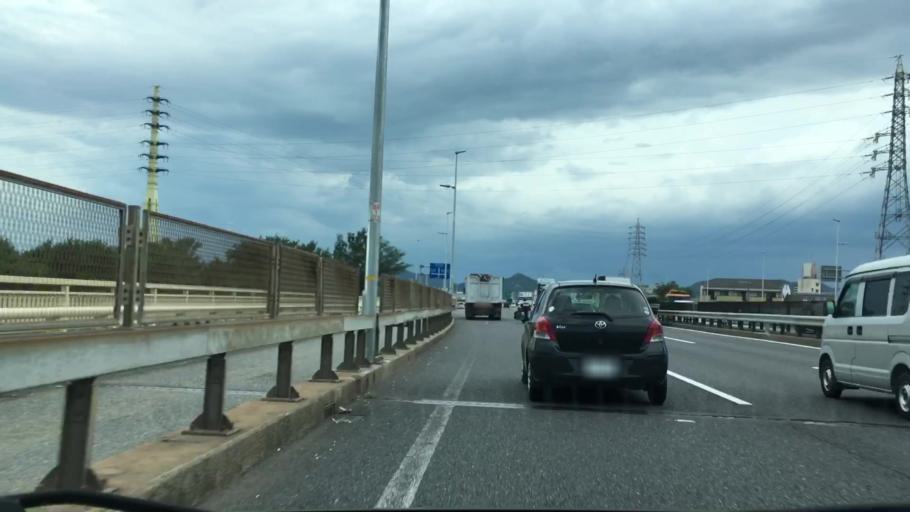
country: JP
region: Hyogo
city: Himeji
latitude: 34.8078
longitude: 134.6948
